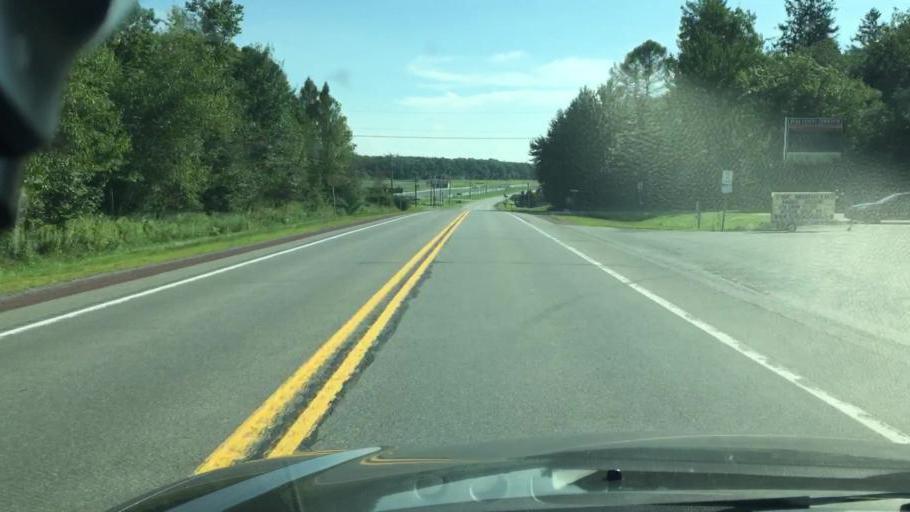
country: US
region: Pennsylvania
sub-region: Carbon County
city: Jim Thorpe
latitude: 40.9370
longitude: -75.6567
